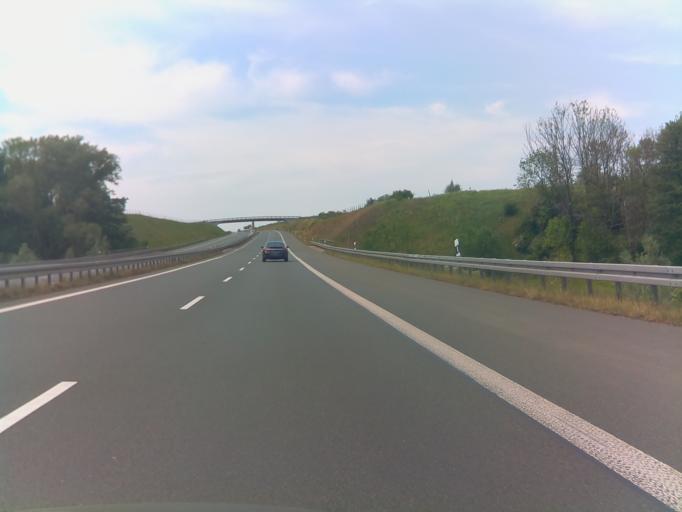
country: DE
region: Saxony-Anhalt
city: Ditfurt
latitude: 51.8107
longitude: 11.1794
